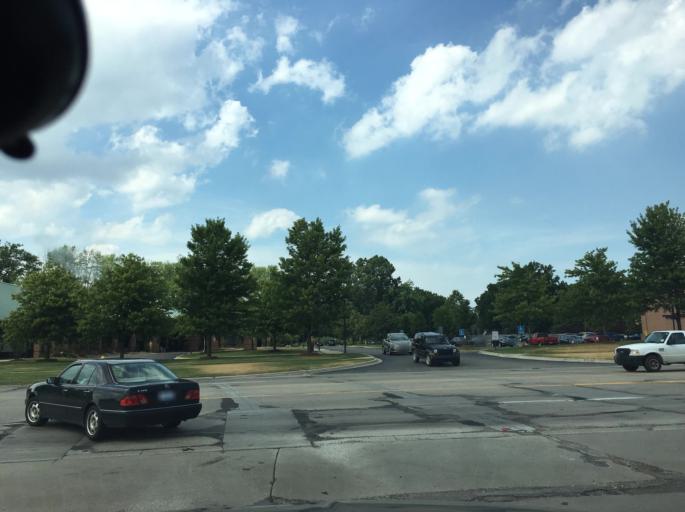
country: US
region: Michigan
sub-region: Macomb County
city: Fraser
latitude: 42.5531
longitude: -82.9643
